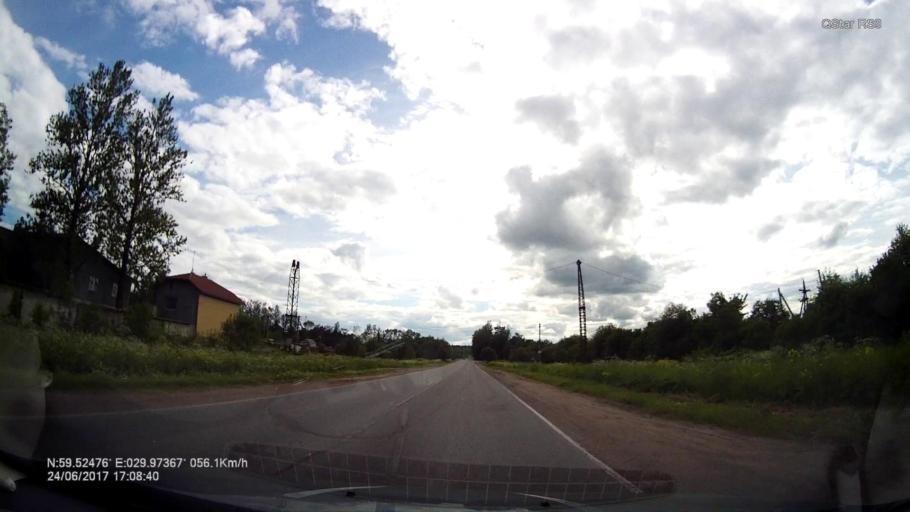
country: RU
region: Leningrad
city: Voyskovitsy
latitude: 59.5245
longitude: 29.9731
